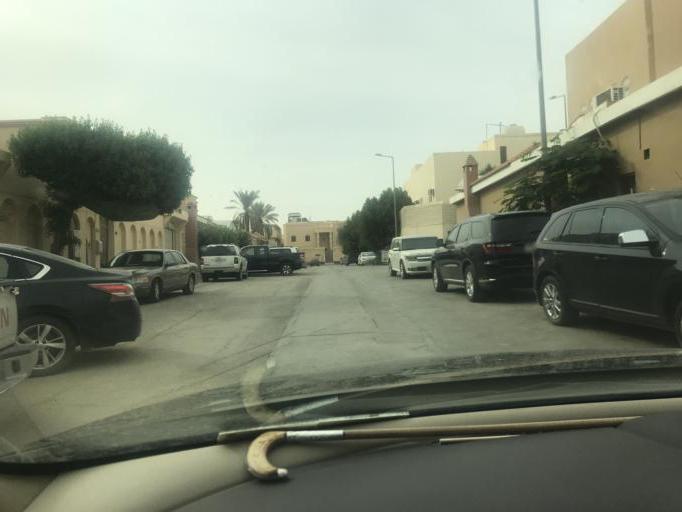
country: SA
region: Ar Riyad
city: Riyadh
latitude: 24.7550
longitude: 46.7668
